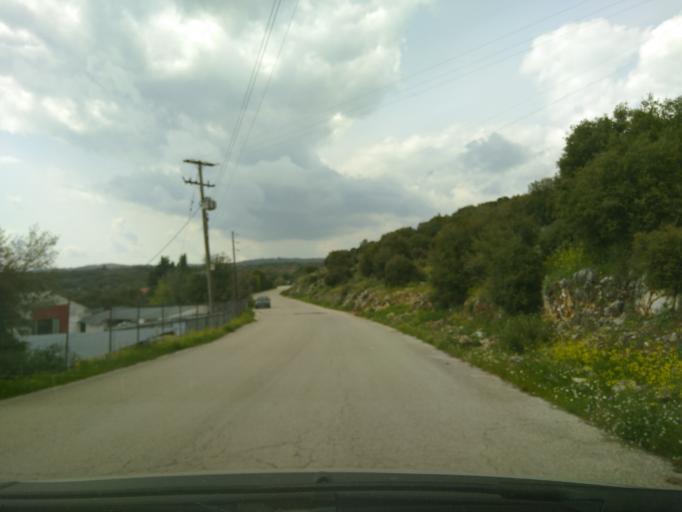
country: GR
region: Epirus
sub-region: Nomos Ioanninon
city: Asprangeloi
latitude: 39.7736
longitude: 20.6911
